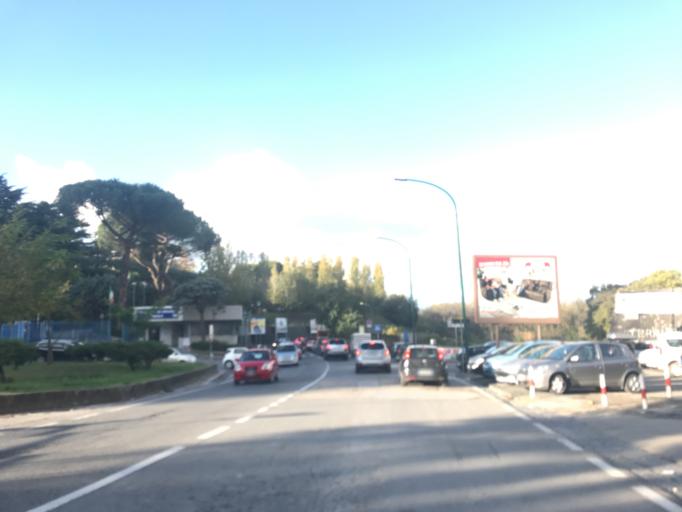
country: IT
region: Campania
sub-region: Provincia di Napoli
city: Napoli
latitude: 40.8703
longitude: 14.2221
